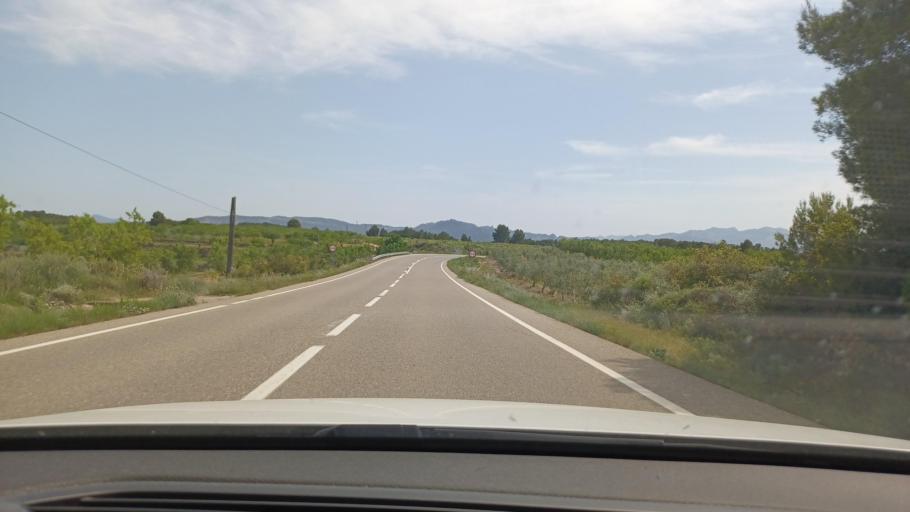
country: ES
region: Catalonia
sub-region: Provincia de Tarragona
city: Vilalba dels Arcs
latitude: 41.0922
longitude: 0.4192
